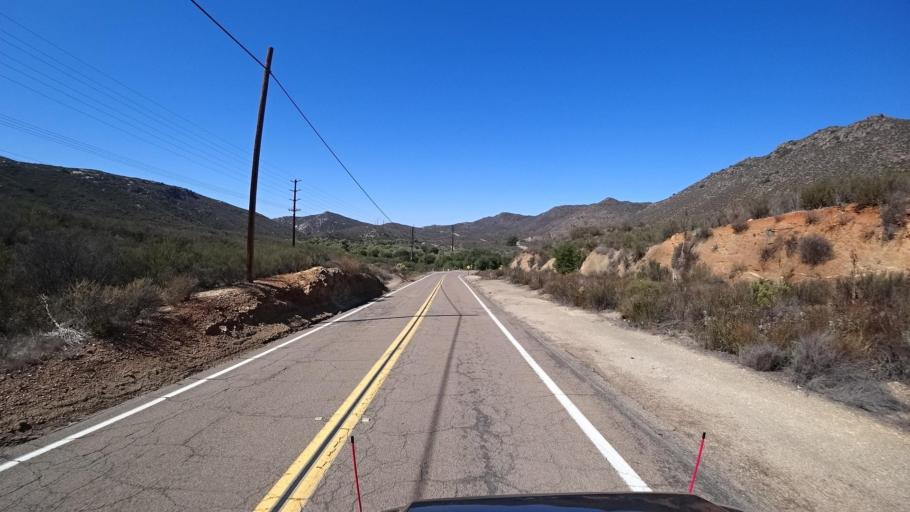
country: US
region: California
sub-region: San Diego County
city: Alpine
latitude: 32.7924
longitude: -116.7402
